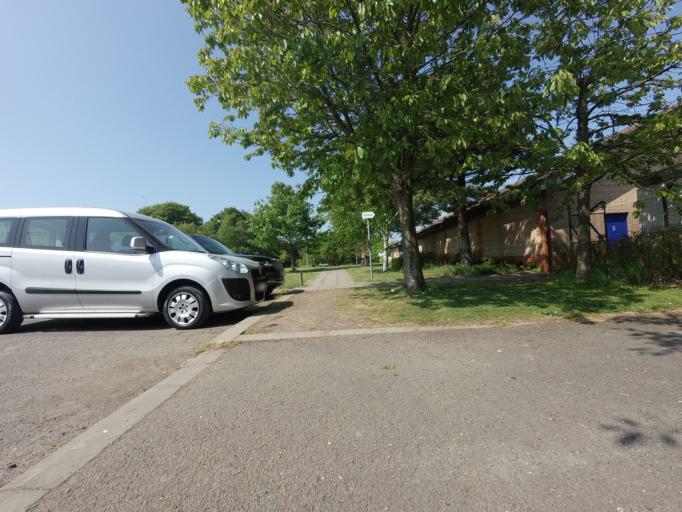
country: GB
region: Scotland
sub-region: Fife
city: Townhill
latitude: 56.0865
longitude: -3.4476
